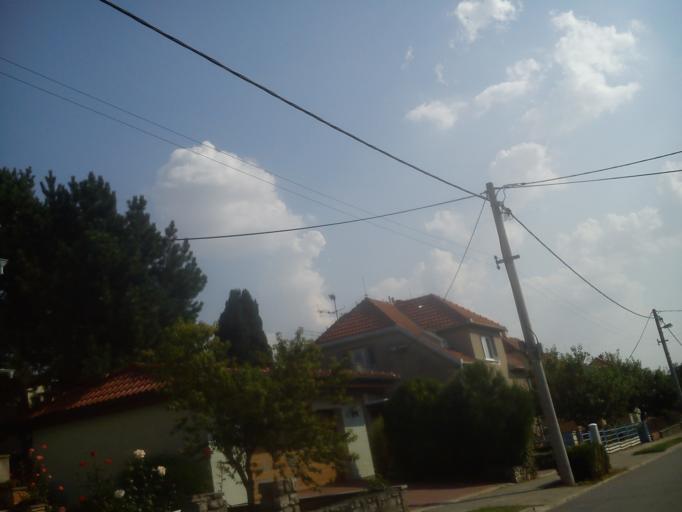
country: CZ
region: South Moravian
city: Sokolnice
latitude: 49.1054
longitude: 16.7479
